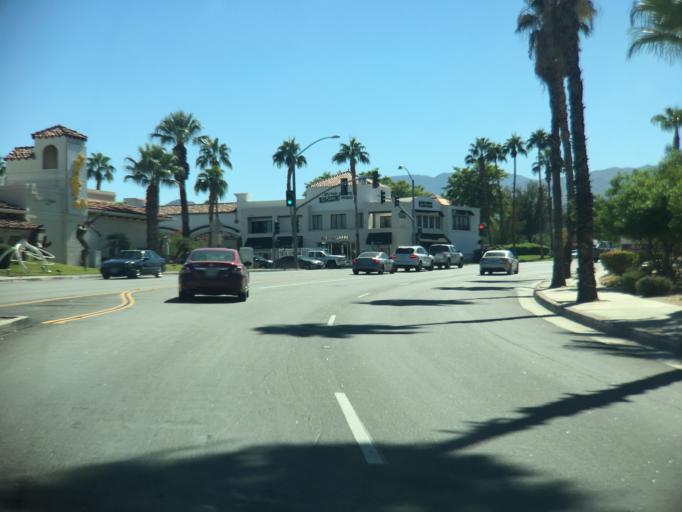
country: US
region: California
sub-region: Riverside County
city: Palm Desert
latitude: 33.7208
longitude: -116.3911
